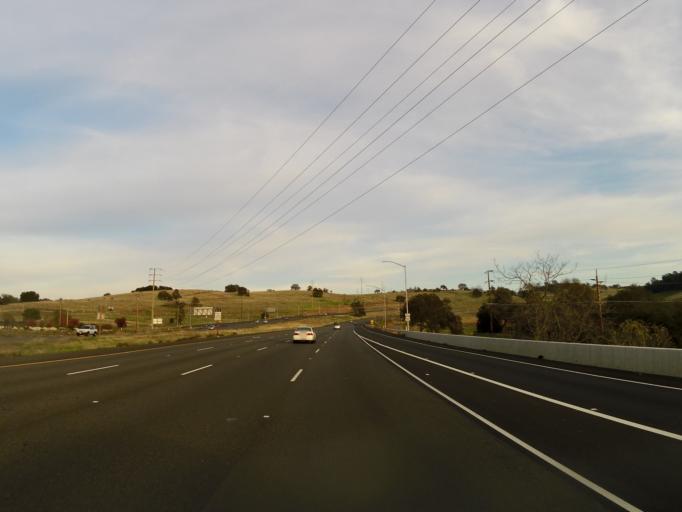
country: US
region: California
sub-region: El Dorado County
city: El Dorado Hills
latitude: 38.6580
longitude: -121.0533
